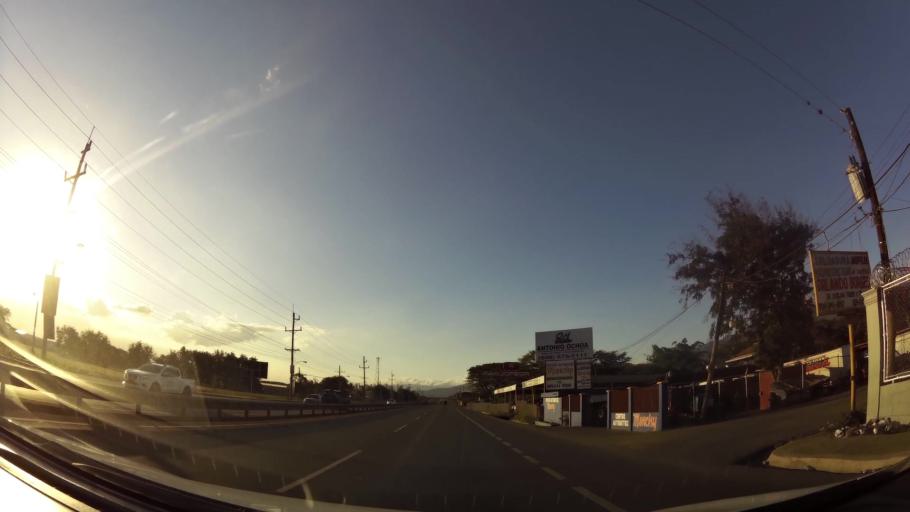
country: DO
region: Santiago
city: Palmar Arriba
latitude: 19.5077
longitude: -70.7545
